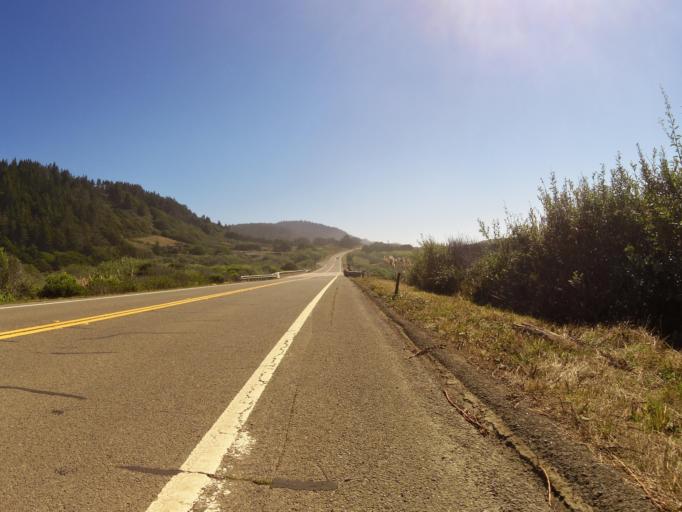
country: US
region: California
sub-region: Mendocino County
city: Fort Bragg
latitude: 39.6600
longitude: -123.7854
